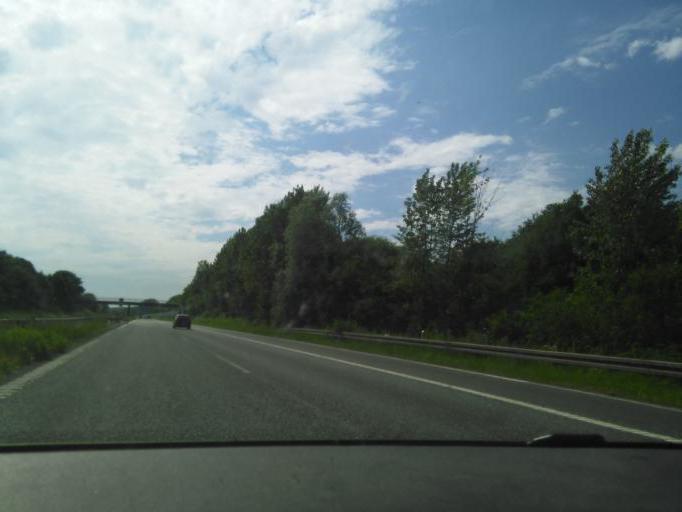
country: DK
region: Zealand
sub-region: Slagelse Kommune
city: Slagelse
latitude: 55.3883
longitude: 11.3552
